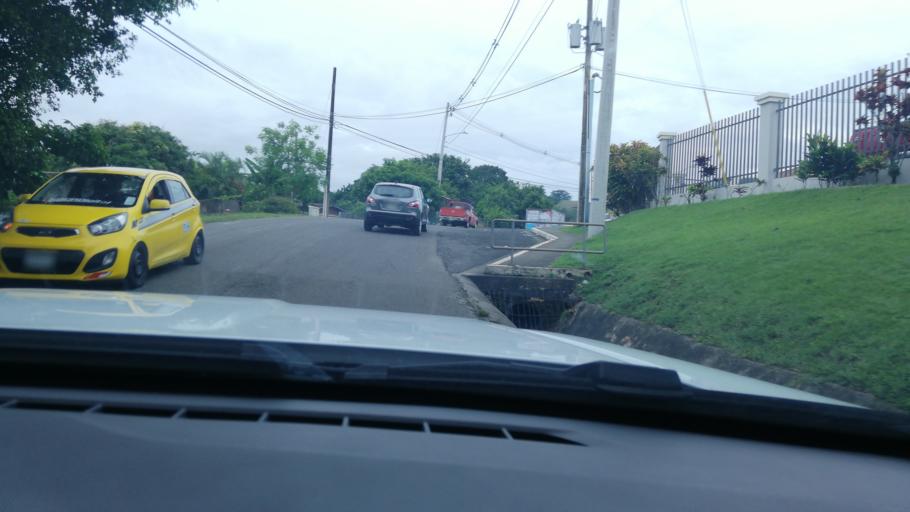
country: PA
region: Panama
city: Las Cumbres
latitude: 9.0746
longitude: -79.5194
